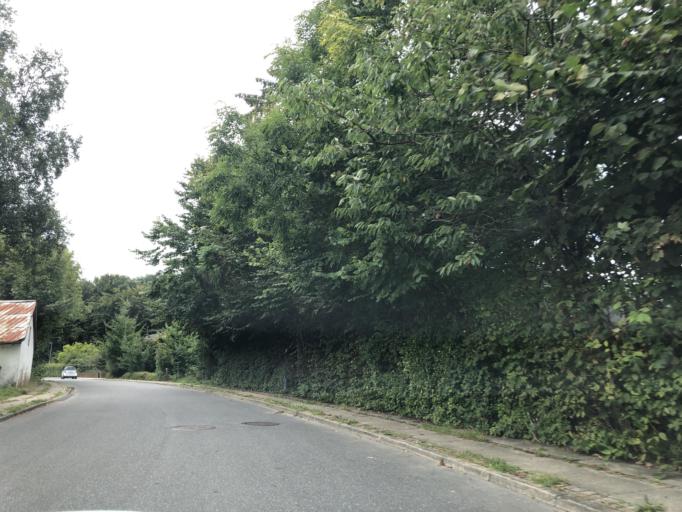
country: DK
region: North Denmark
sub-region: Alborg Kommune
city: Nibe
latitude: 56.8505
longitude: 9.6969
